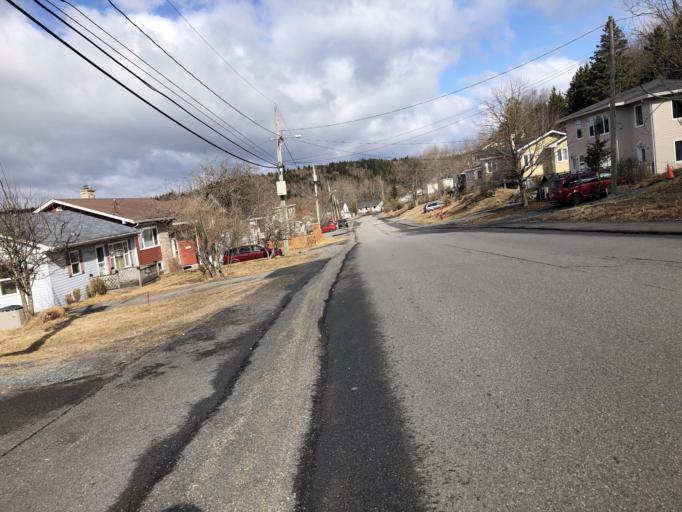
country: CA
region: New Brunswick
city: Saint John
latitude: 45.3199
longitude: -66.0096
